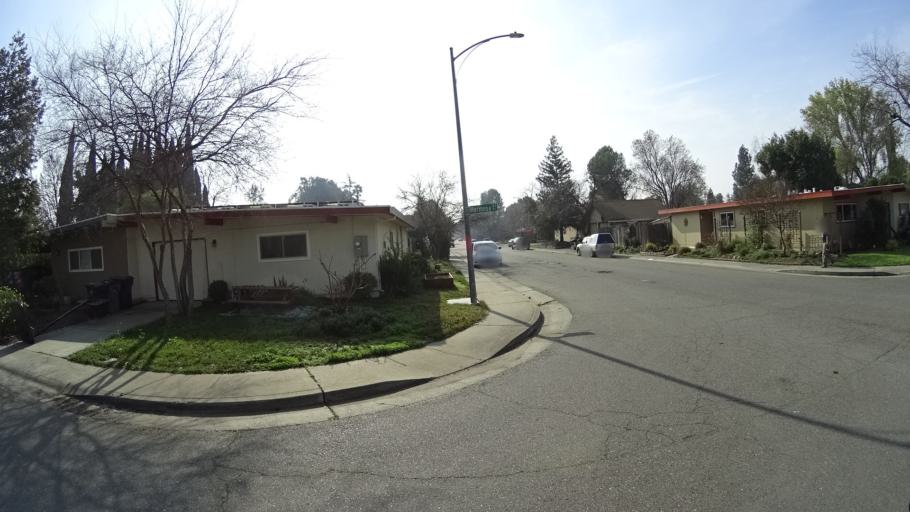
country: US
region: California
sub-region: Yolo County
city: Davis
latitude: 38.5689
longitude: -121.7567
